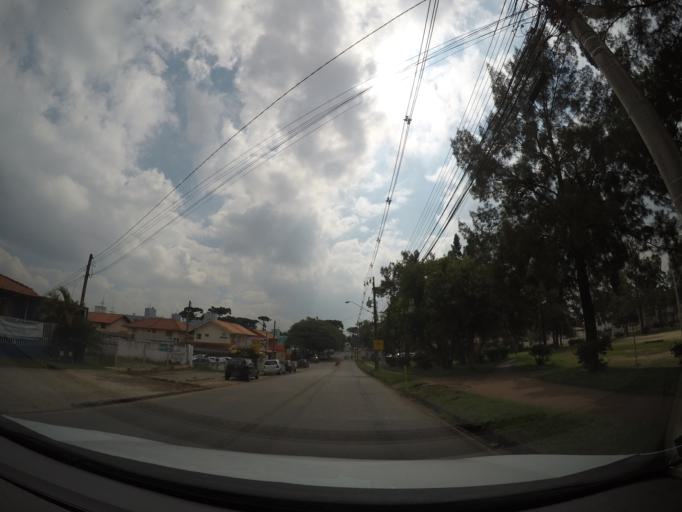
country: BR
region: Parana
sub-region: Sao Jose Dos Pinhais
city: Sao Jose dos Pinhais
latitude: -25.5050
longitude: -49.2483
